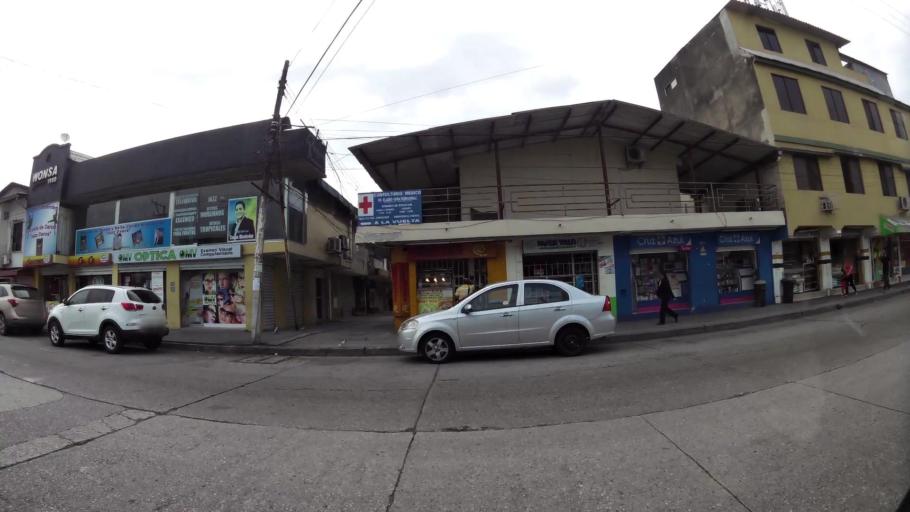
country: EC
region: Guayas
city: Eloy Alfaro
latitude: -2.1365
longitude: -79.8893
